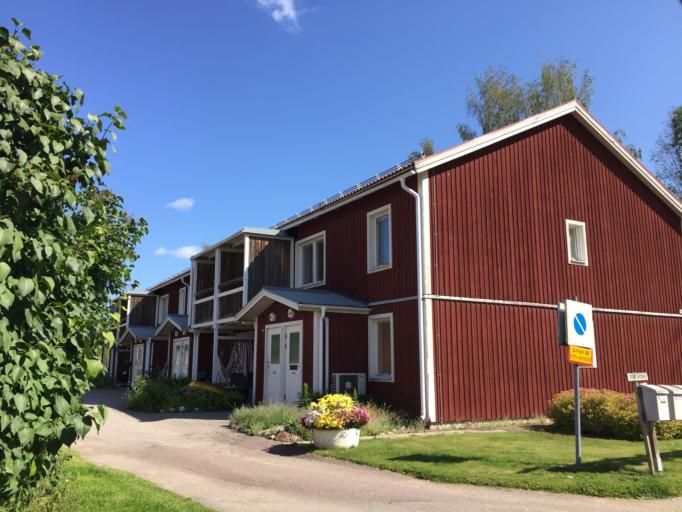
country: SE
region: Dalarna
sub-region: Ludvika Kommun
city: Grangesberg
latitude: 60.2613
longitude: 14.9788
